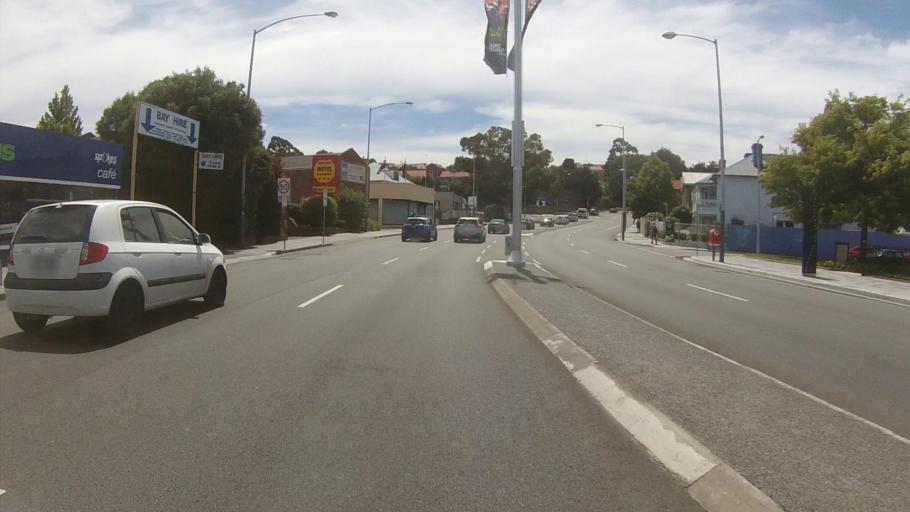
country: AU
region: Tasmania
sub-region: Hobart
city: Sandy Bay
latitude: -42.8932
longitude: 147.3258
